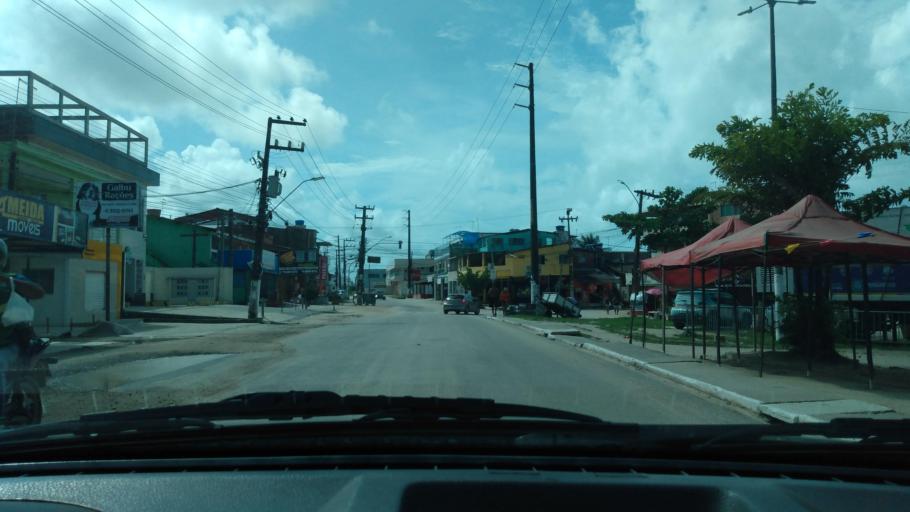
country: BR
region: Pernambuco
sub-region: Cabo De Santo Agostinho
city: Cabo
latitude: -8.3376
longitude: -34.9540
